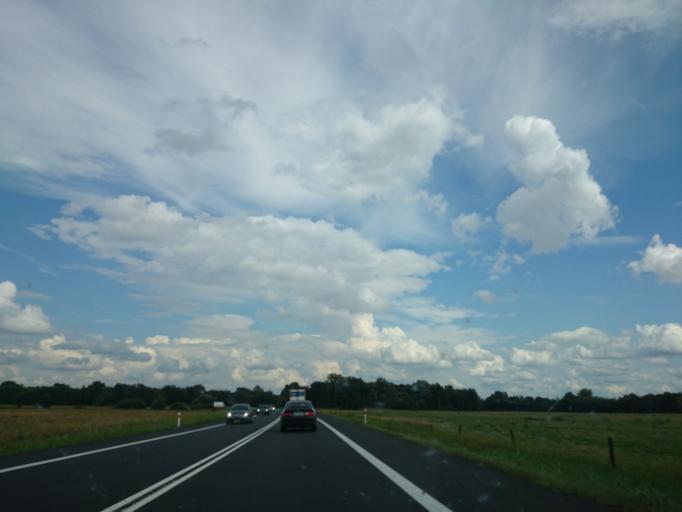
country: PL
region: Lubusz
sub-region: Powiat zielonogorski
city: Sulechow
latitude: 52.0112
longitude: 15.6179
